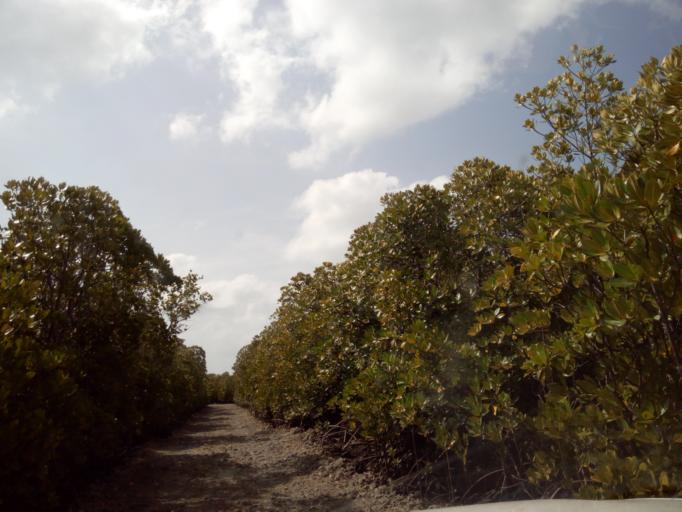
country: TZ
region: Zanzibar Central/South
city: Mahonda
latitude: -6.3179
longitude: 39.3867
